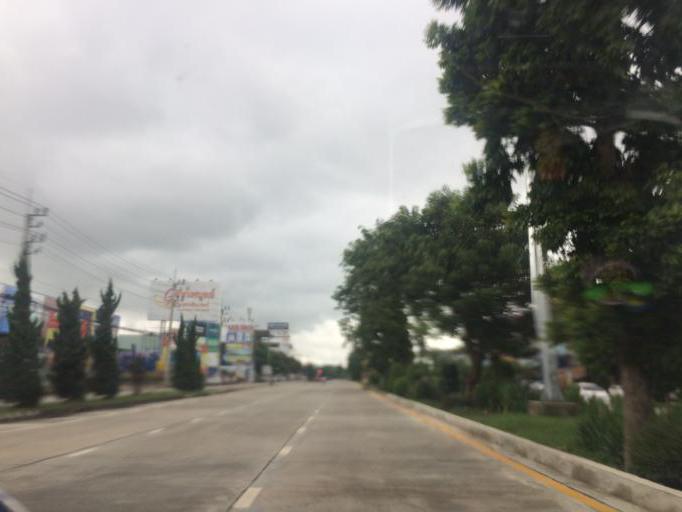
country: TH
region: Chiang Rai
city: Chiang Rai
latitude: 19.9003
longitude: 99.8395
